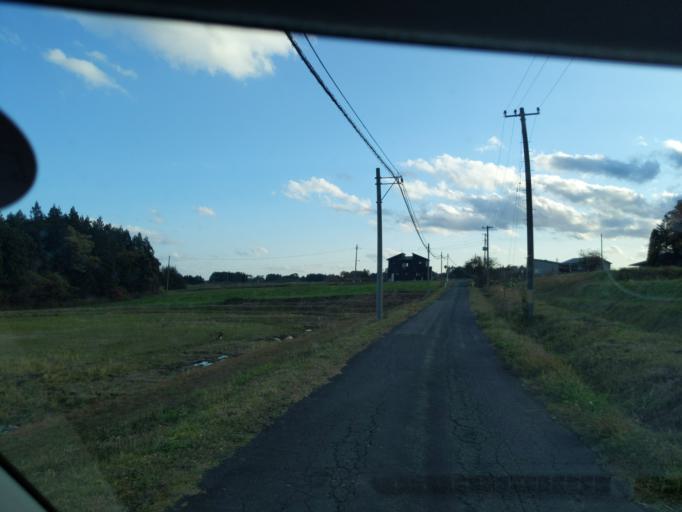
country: JP
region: Iwate
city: Mizusawa
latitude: 39.1031
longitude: 141.0395
